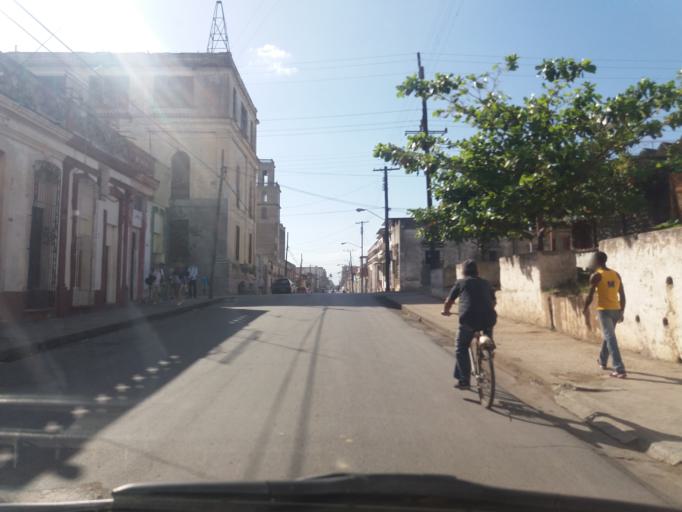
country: CU
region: Cienfuegos
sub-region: Municipio de Cienfuegos
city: Cienfuegos
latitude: 22.1454
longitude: -80.4432
